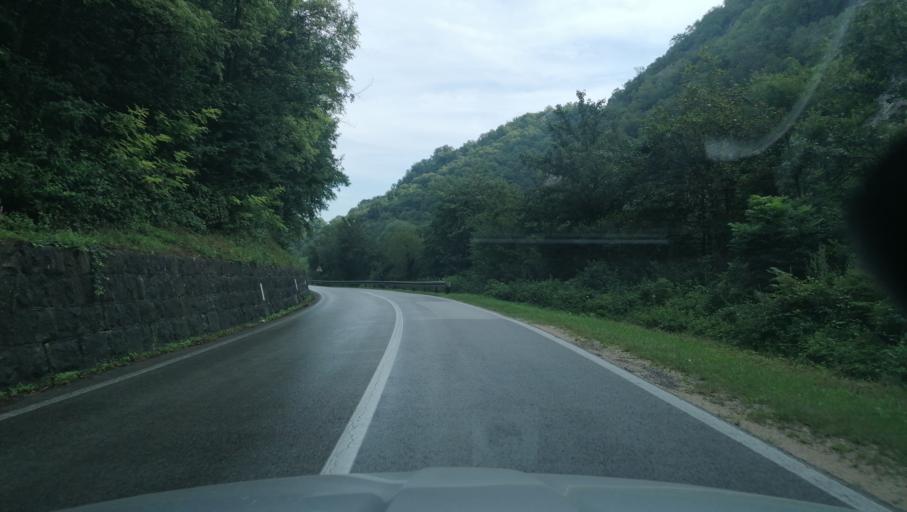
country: BA
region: Republika Srpska
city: Hiseti
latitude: 44.6542
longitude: 17.1457
